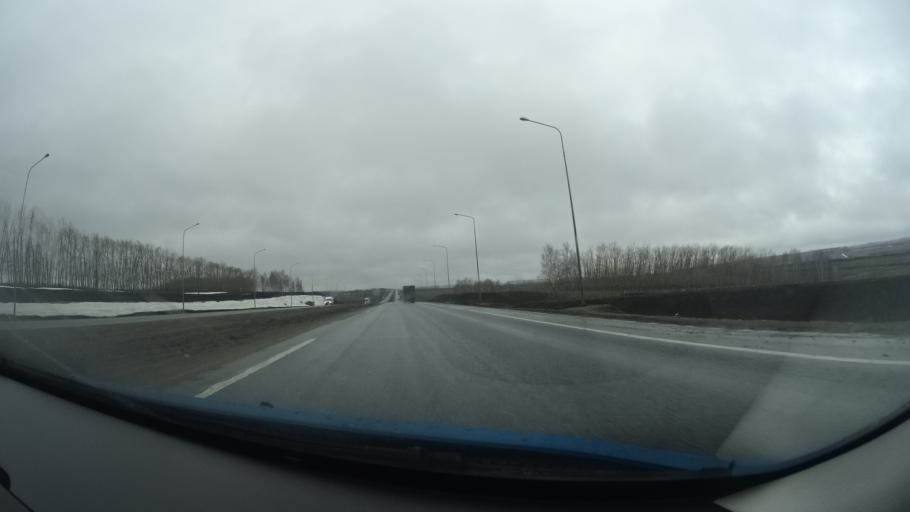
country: RU
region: Bashkortostan
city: Alekseyevka
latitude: 54.7196
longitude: 54.9021
